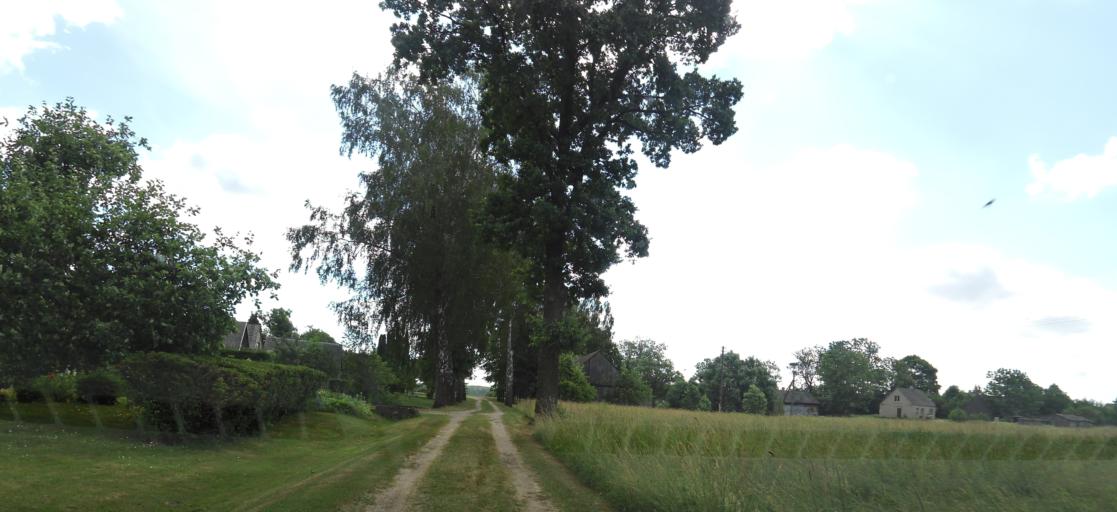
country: LT
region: Panevezys
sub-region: Birzai
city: Birzai
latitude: 56.1074
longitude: 24.8095
